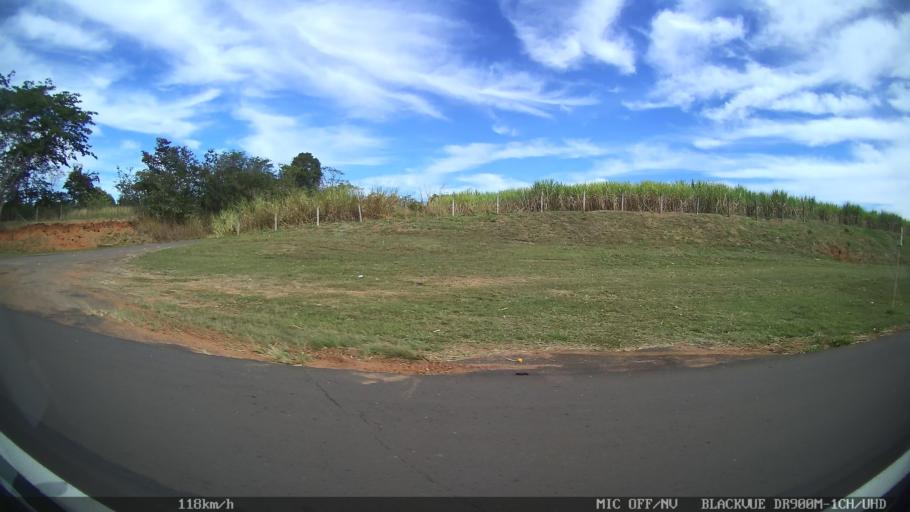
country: BR
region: Sao Paulo
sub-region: Taquaritinga
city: Taquaritinga
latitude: -21.4508
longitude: -48.6347
